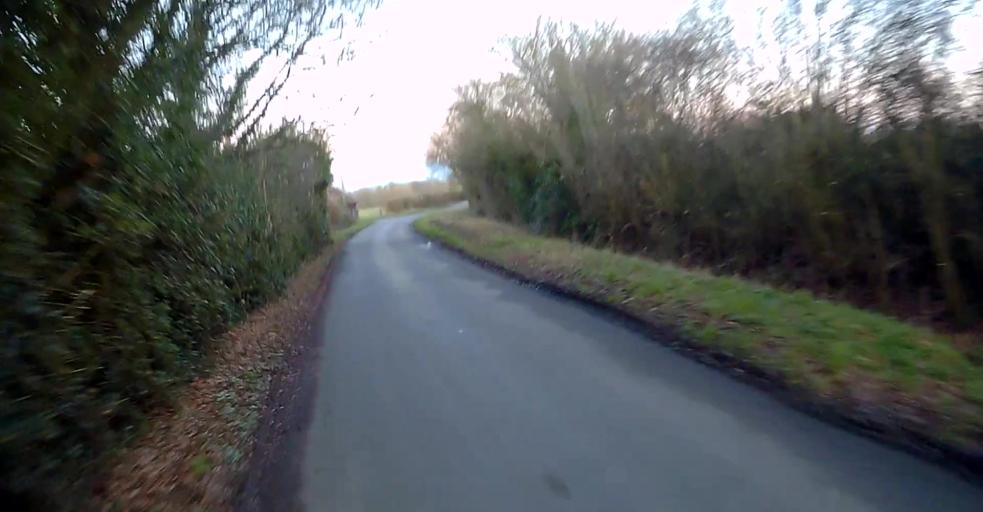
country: GB
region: England
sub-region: West Berkshire
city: Stratfield Mortimer
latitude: 51.3348
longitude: -1.0556
